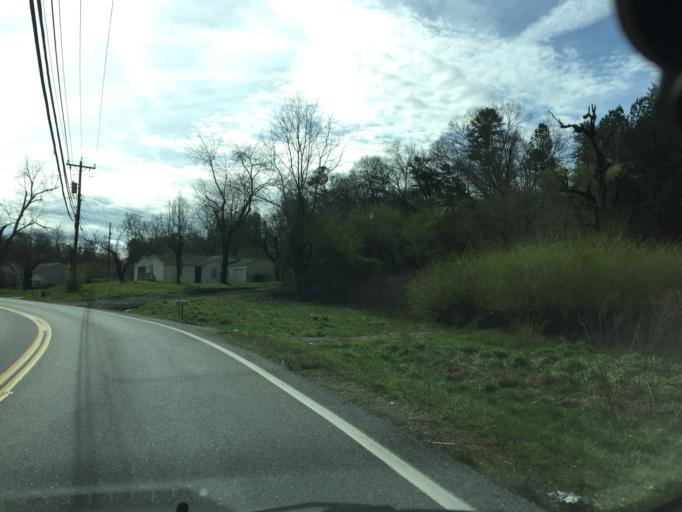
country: US
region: Tennessee
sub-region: Hamilton County
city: East Brainerd
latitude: 35.0403
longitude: -85.1127
